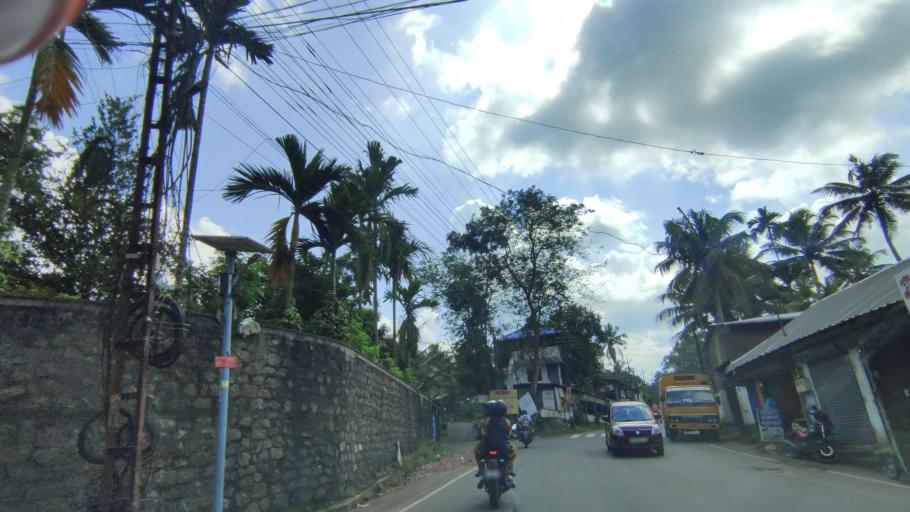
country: IN
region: Kerala
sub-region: Kottayam
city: Kottayam
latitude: 9.6757
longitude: 76.5391
